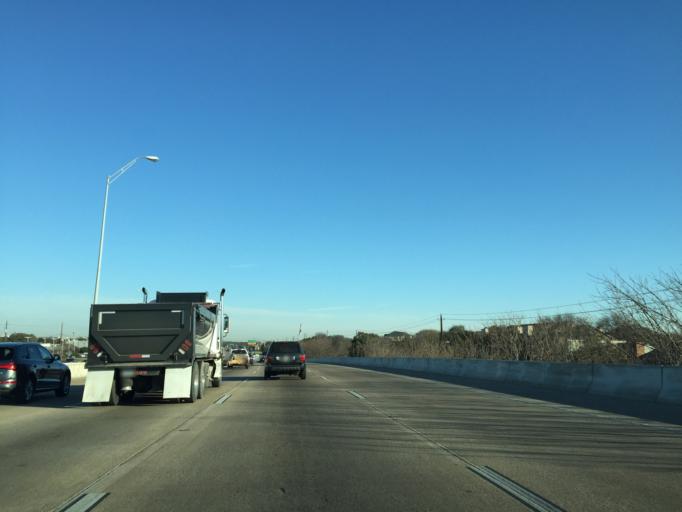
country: US
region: Texas
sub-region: Williamson County
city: Jollyville
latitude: 30.4094
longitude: -97.7450
